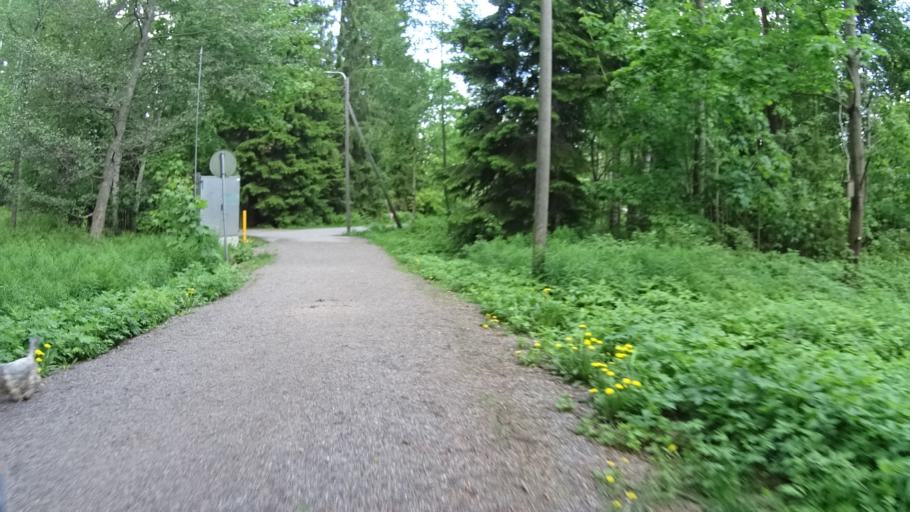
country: FI
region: Uusimaa
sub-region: Helsinki
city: Kauniainen
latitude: 60.2181
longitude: 24.7343
